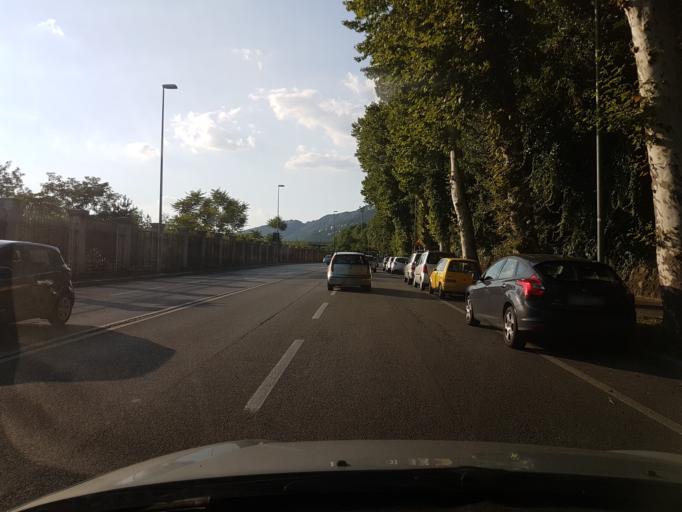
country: IT
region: Friuli Venezia Giulia
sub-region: Provincia di Trieste
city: Villa Opicina
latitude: 45.6711
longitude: 13.7584
